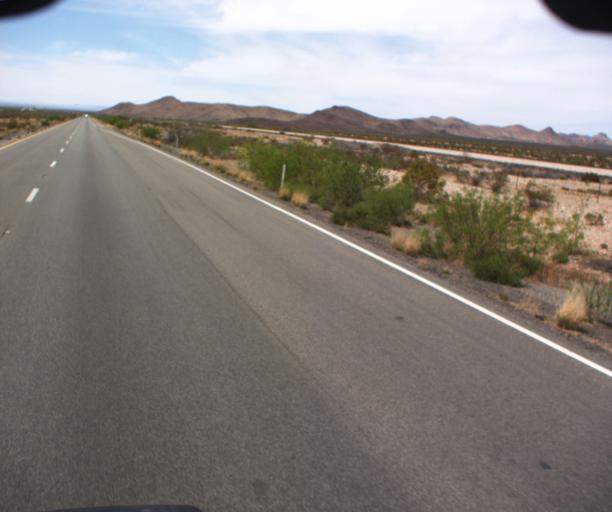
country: US
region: New Mexico
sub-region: Hidalgo County
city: Lordsburg
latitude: 32.2310
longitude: -109.0600
